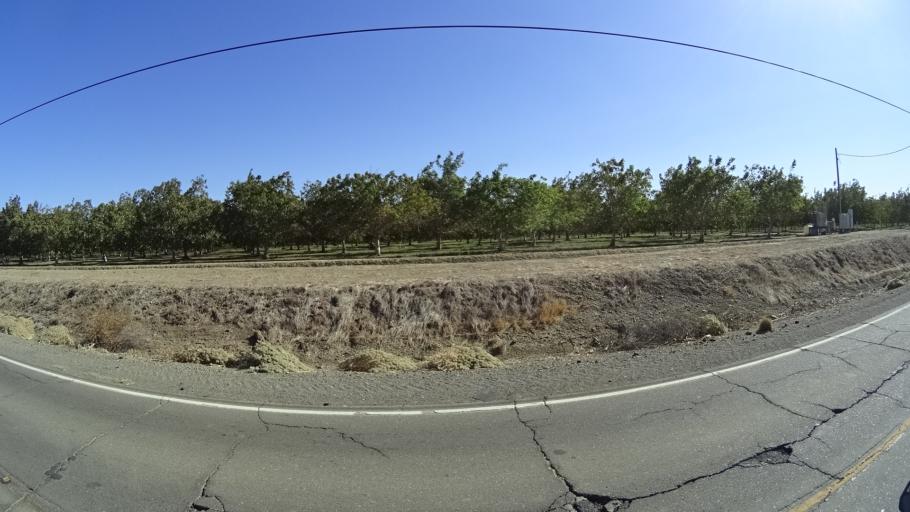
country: US
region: California
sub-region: Yolo County
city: Cottonwood
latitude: 38.5956
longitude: -121.9715
